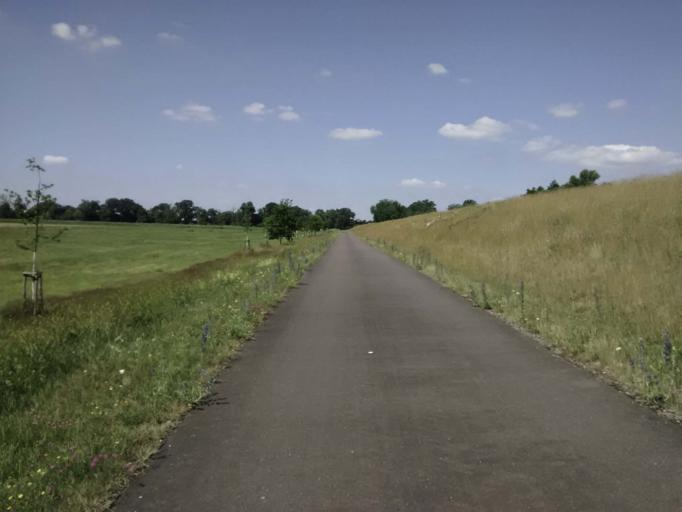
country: DE
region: Saxony-Anhalt
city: Worlitz
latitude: 51.8407
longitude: 12.4663
